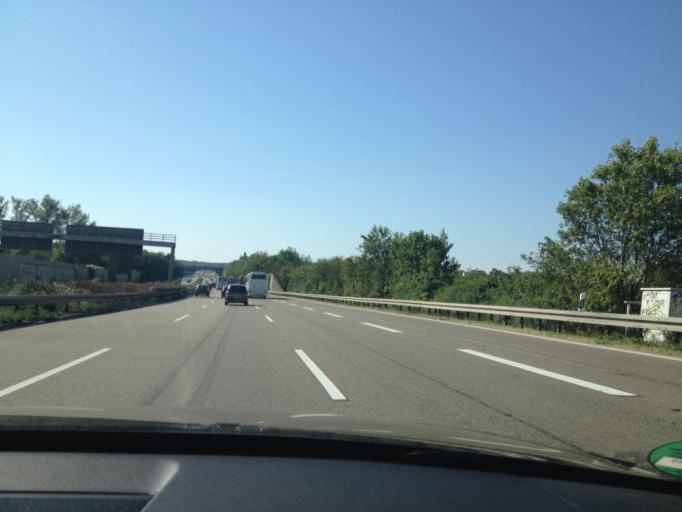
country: DE
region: Baden-Wuerttemberg
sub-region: Regierungsbezirk Stuttgart
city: Asperg
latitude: 48.9141
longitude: 9.1544
